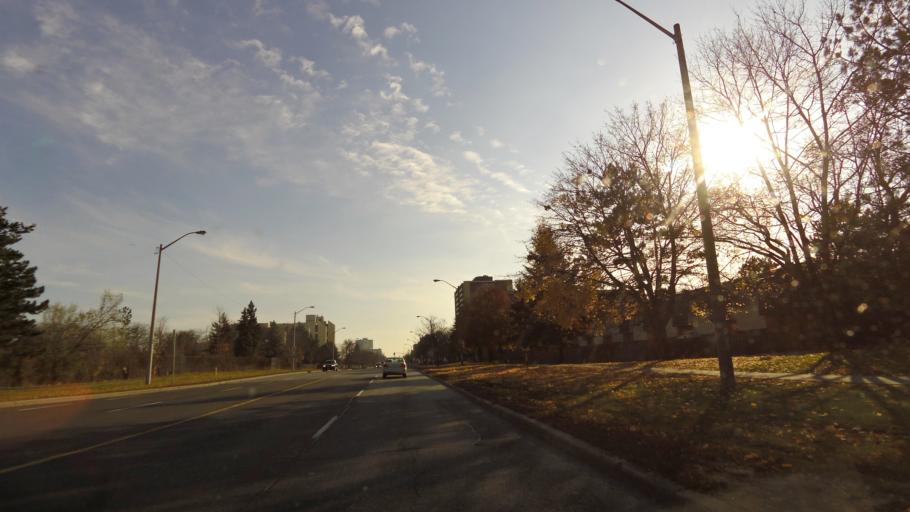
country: CA
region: Ontario
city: Concord
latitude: 43.7730
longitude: -79.5214
